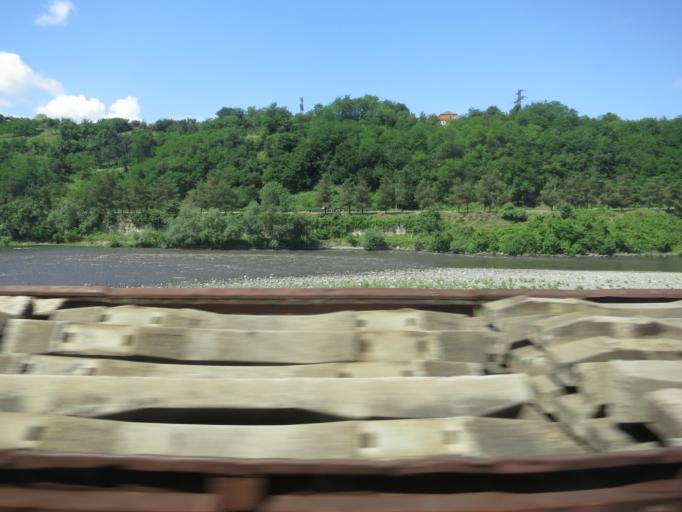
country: GE
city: Shorapani
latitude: 42.0983
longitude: 43.0766
